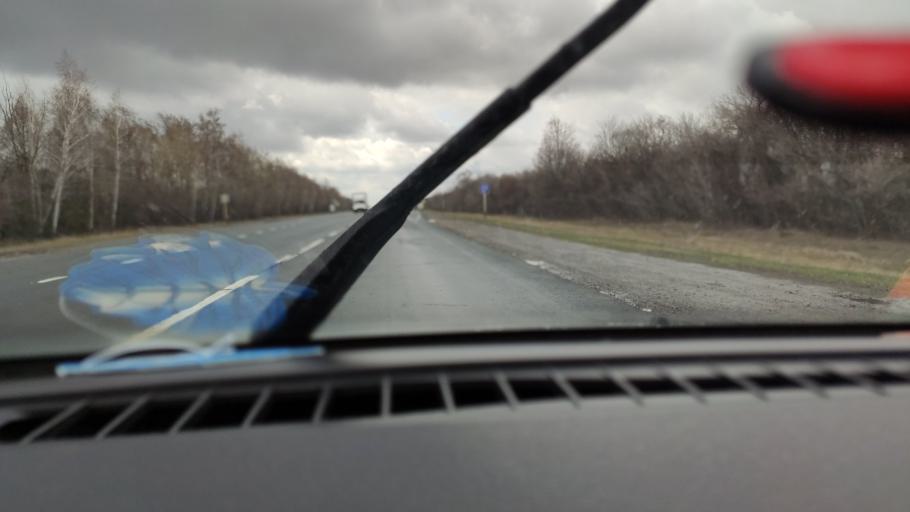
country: RU
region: Samara
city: Yelkhovka
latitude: 53.9419
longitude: 50.2647
